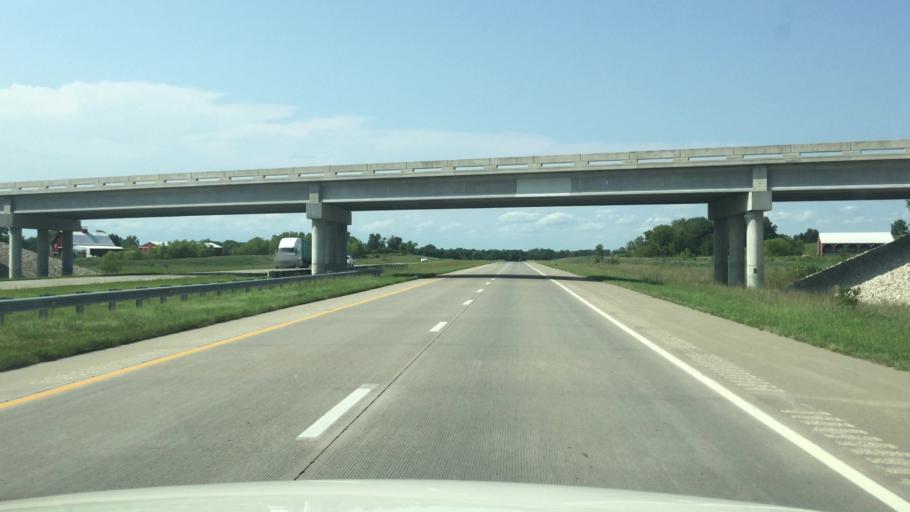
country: US
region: Kansas
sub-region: Linn County
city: La Cygne
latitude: 38.2865
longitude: -94.6733
